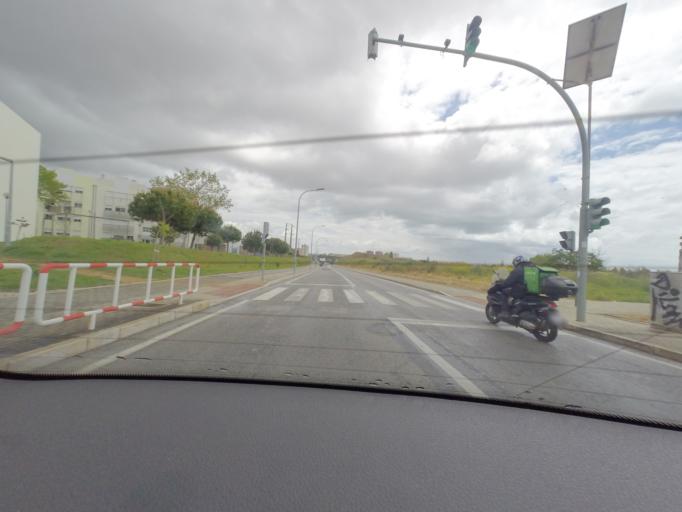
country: PT
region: Lisbon
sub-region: Cascais
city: Sao Domingos de Rana
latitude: 38.6981
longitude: -9.3391
